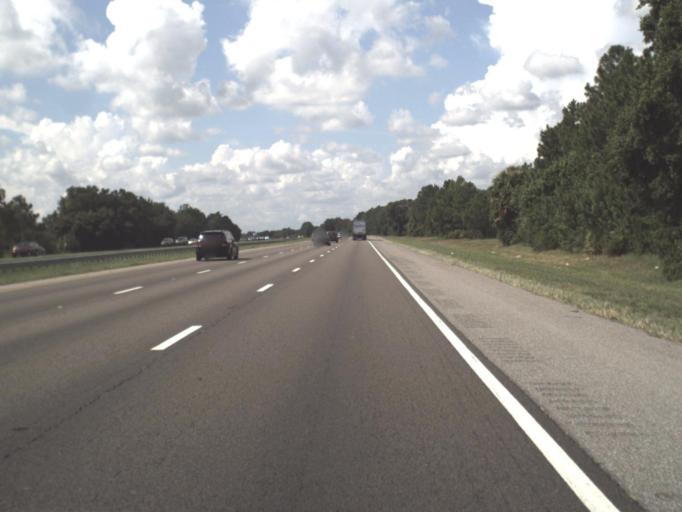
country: US
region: Florida
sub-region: Hillsborough County
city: Gibsonton
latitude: 27.8279
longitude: -82.3513
